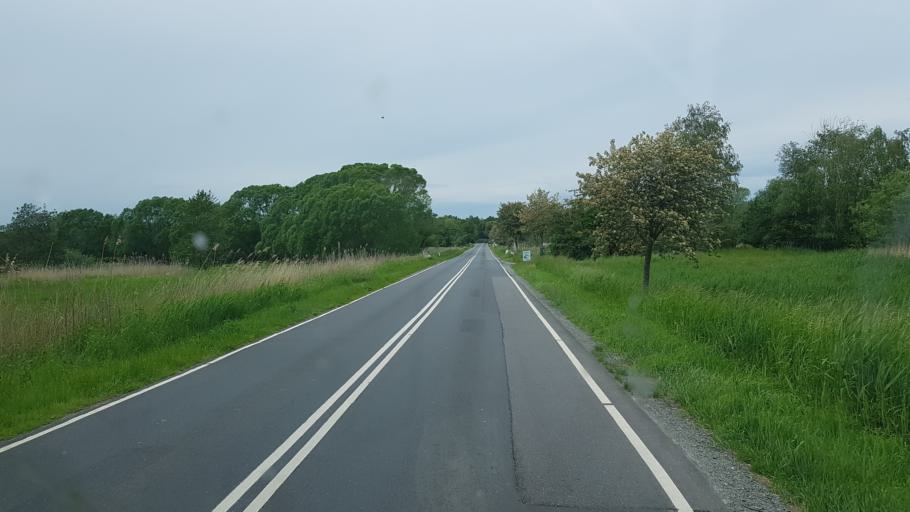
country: DK
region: South Denmark
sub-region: Nordfyns Kommune
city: Sonderso
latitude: 55.5716
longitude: 10.2038
